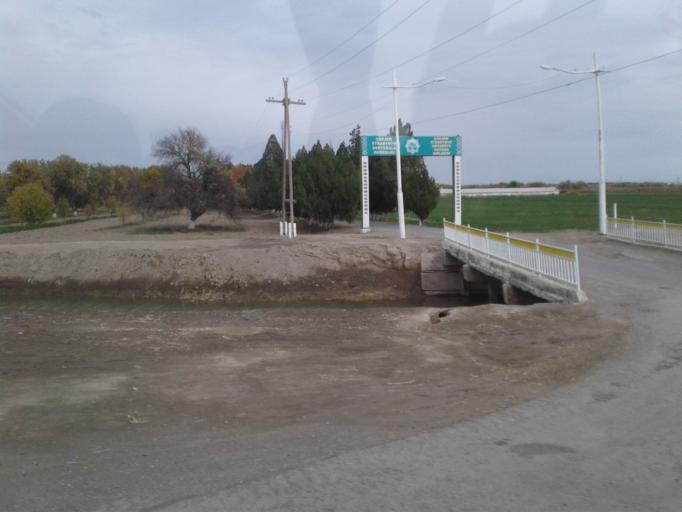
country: TM
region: Lebap
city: Turkmenabat
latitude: 39.1531
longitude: 63.3908
